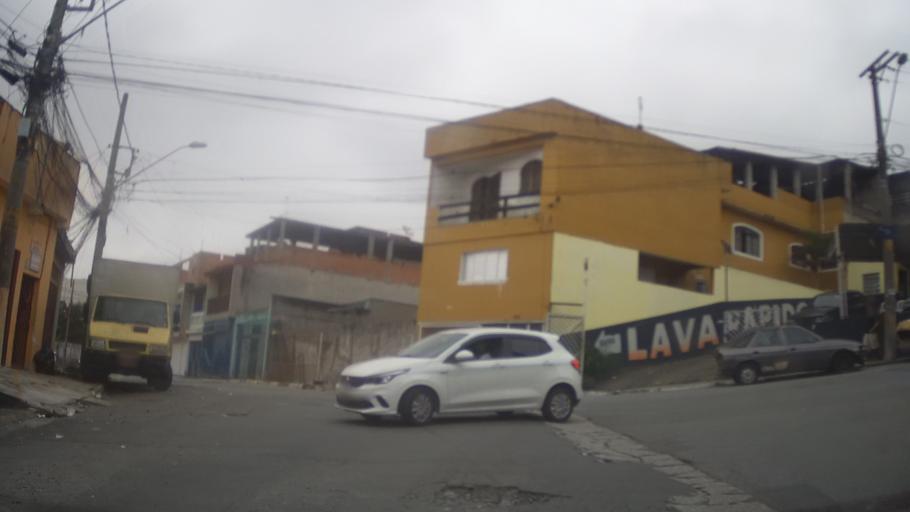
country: BR
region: Sao Paulo
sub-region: Guarulhos
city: Guarulhos
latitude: -23.4297
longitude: -46.5141
